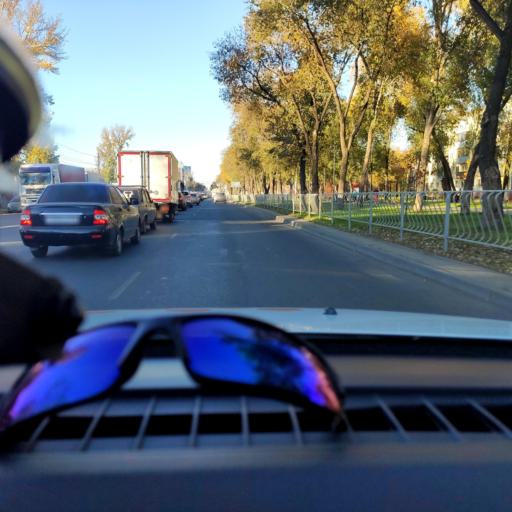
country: RU
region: Samara
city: Samara
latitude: 53.1948
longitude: 50.1907
